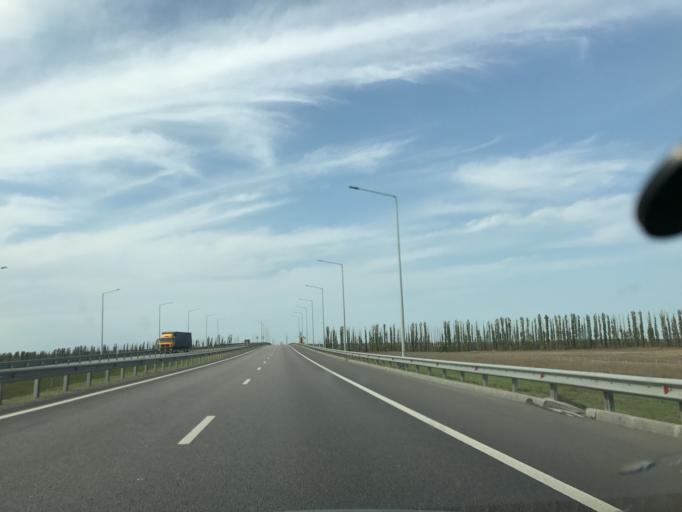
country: RU
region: Voronezj
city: Kashirskoye
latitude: 51.4799
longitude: 39.5505
